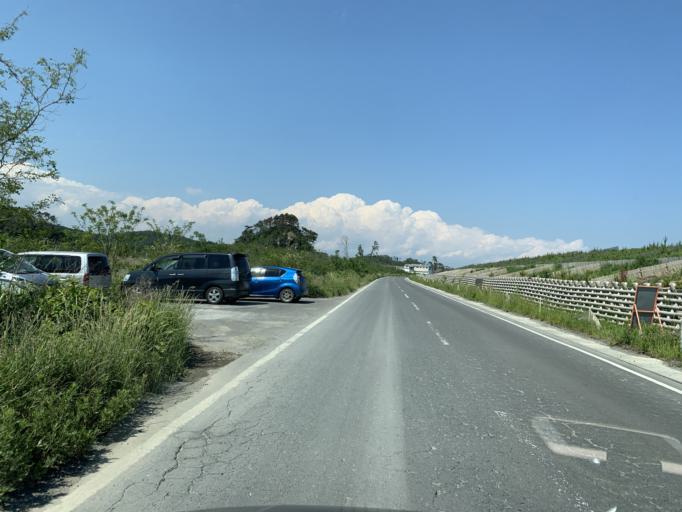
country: JP
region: Miyagi
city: Yamoto
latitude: 38.3667
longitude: 141.1586
